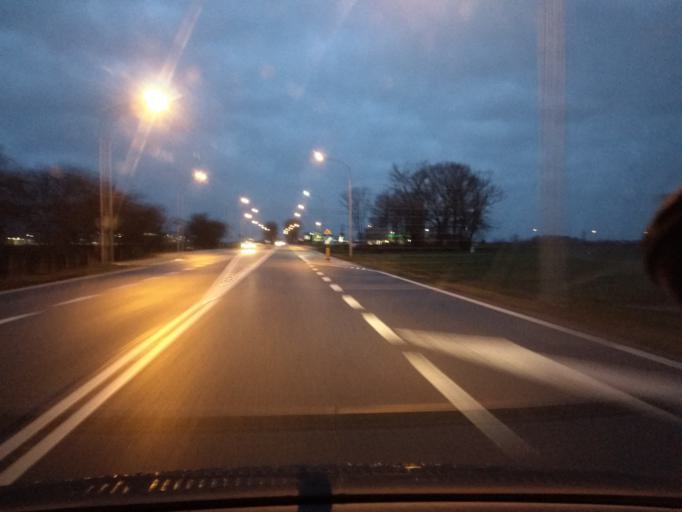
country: PL
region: Lower Silesian Voivodeship
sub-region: Powiat sredzki
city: Mrozow
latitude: 51.1531
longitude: 16.8178
